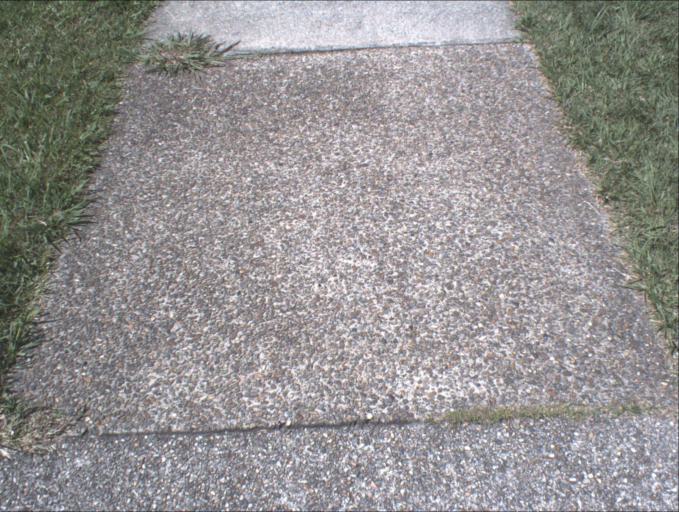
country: AU
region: Queensland
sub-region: Logan
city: Beenleigh
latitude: -27.6986
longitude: 153.1711
